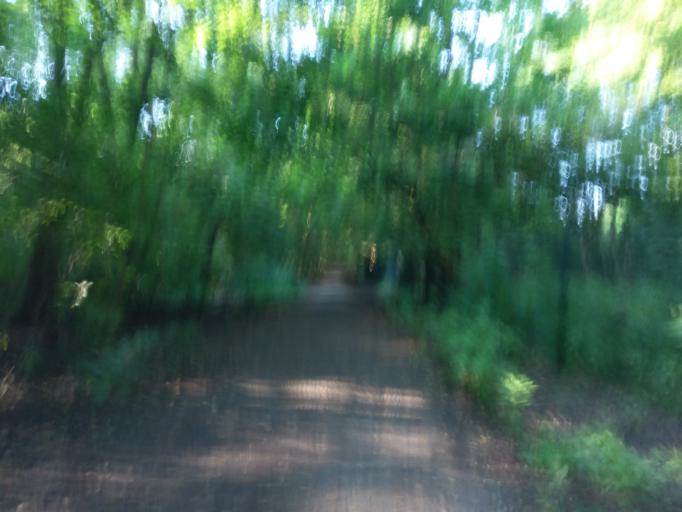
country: DE
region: Brandenburg
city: Teltow
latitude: 52.4150
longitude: 13.2482
